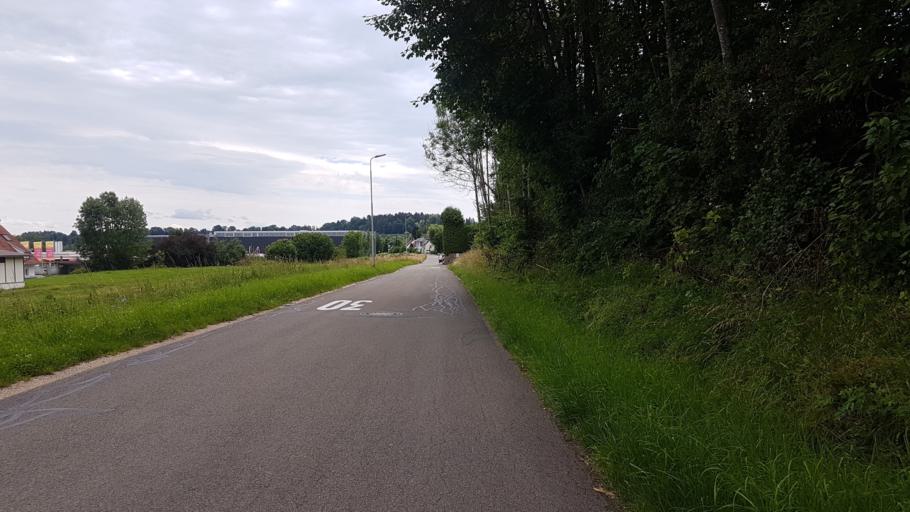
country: DE
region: Baden-Wuerttemberg
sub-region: Tuebingen Region
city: Scheer
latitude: 48.0654
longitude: 9.2966
